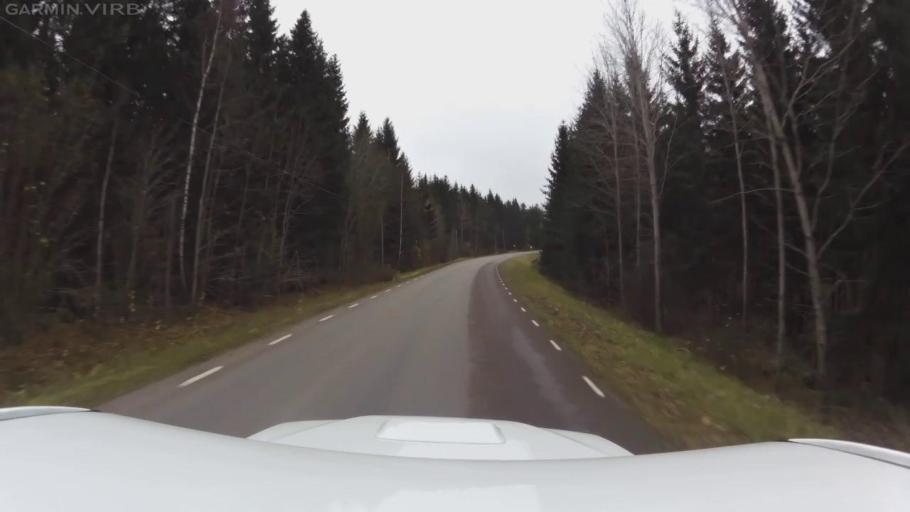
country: SE
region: OEstergoetland
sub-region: Linkopings Kommun
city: Vikingstad
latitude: 58.2511
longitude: 15.3857
